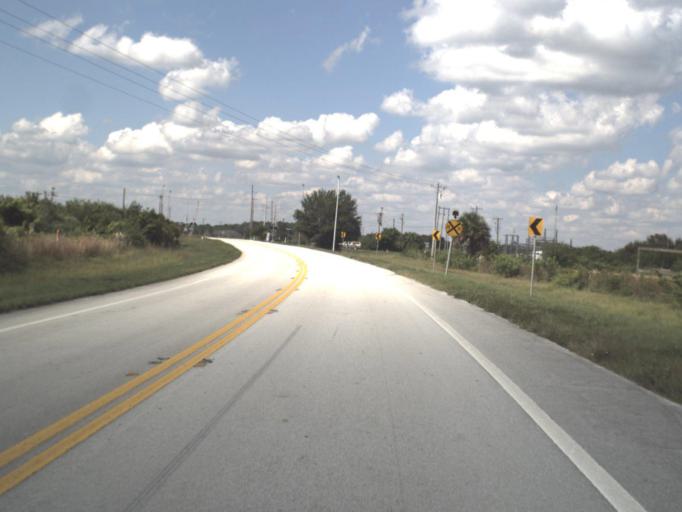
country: US
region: Florida
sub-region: Highlands County
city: Lake Placid
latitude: 27.4373
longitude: -81.2381
